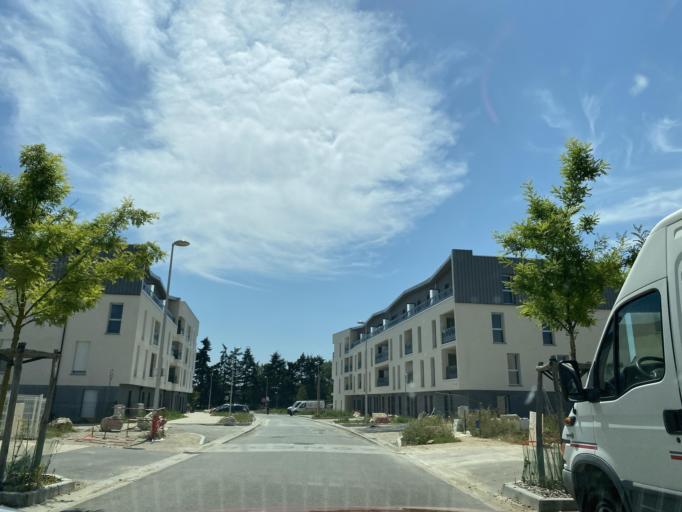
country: FR
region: Centre
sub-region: Departement d'Eure-et-Loir
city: Mainvilliers
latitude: 48.4578
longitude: 1.4545
